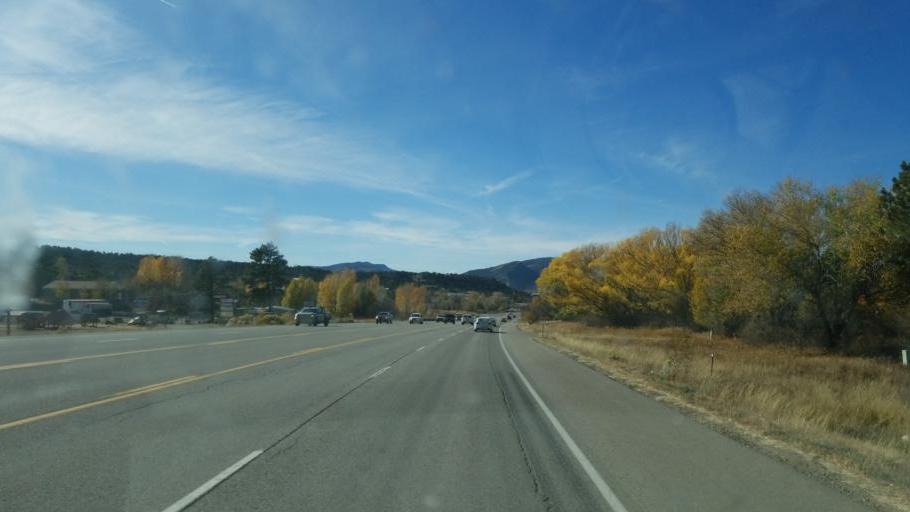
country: US
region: Colorado
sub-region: La Plata County
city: Durango
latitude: 37.2271
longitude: -107.8142
